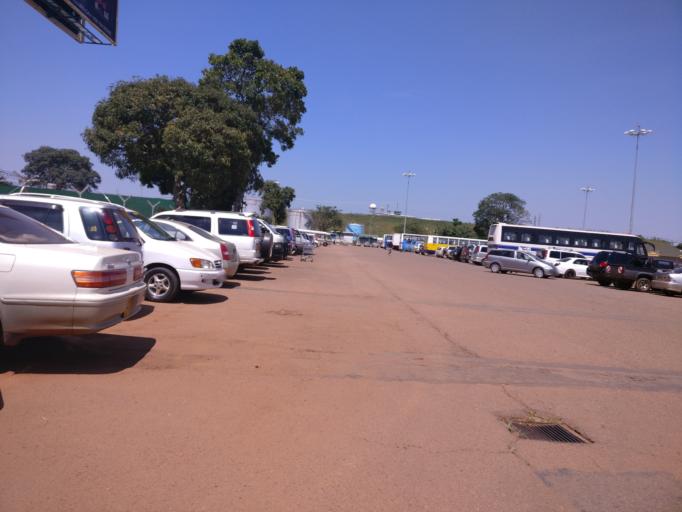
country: UG
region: Central Region
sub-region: Wakiso District
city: Entebbe
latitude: 0.0451
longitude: 32.4444
